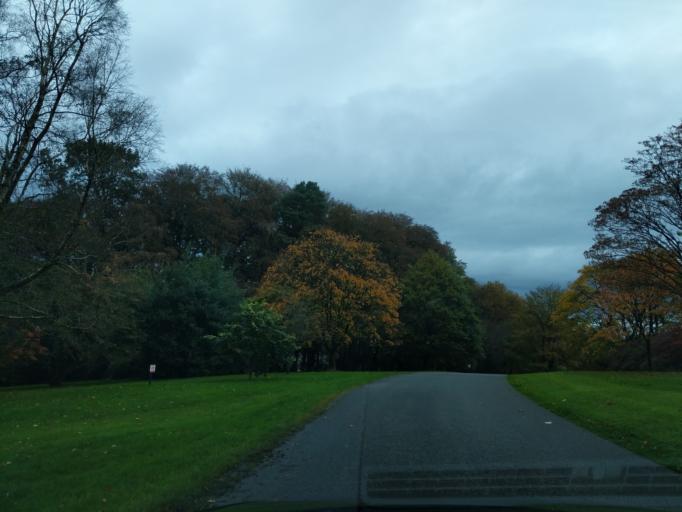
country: GB
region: Scotland
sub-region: Dumfries and Galloway
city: Castle Douglas
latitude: 54.9259
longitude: -3.9468
